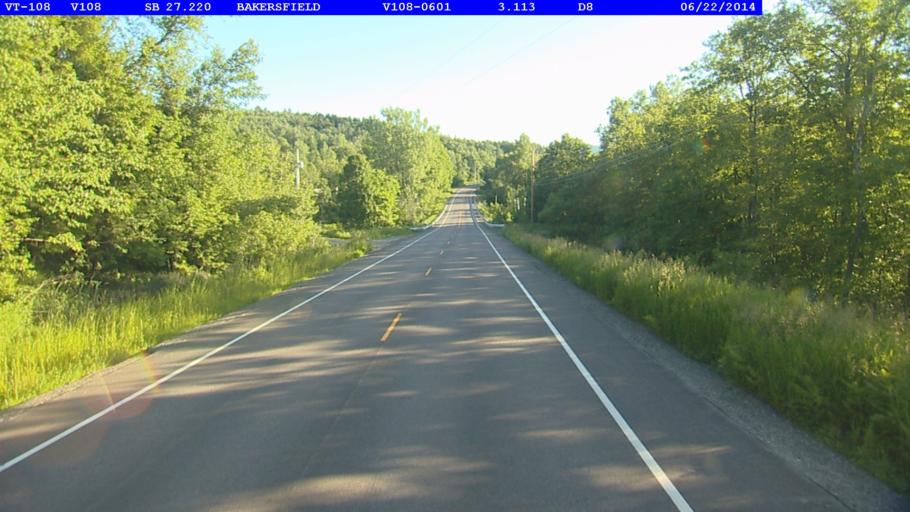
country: US
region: Vermont
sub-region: Franklin County
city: Enosburg Falls
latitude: 44.7747
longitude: -72.8061
